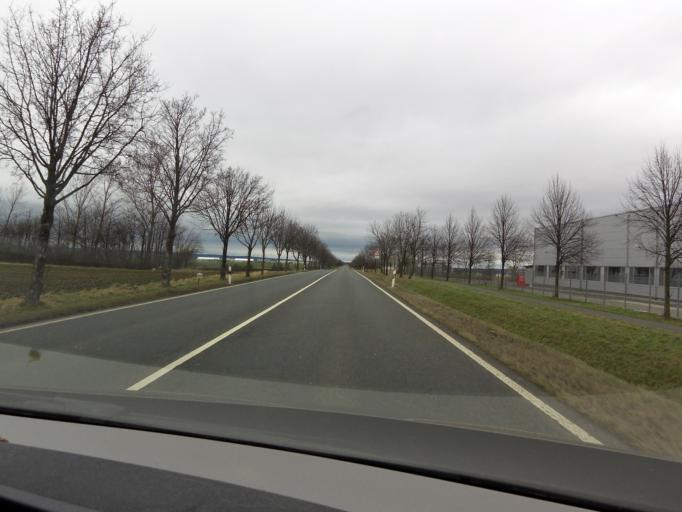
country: DE
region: Thuringia
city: Wiegendorf
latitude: 51.0039
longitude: 11.4538
